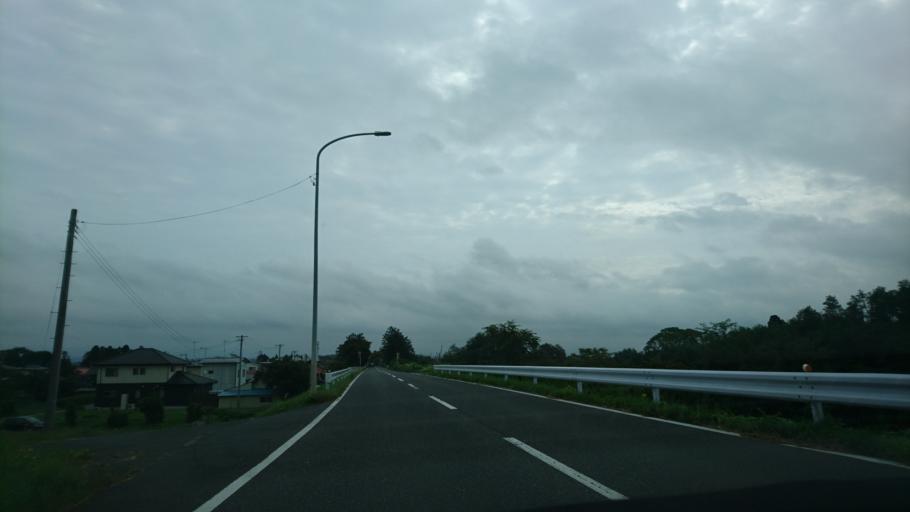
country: JP
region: Iwate
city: Ichinoseki
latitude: 38.7771
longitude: 141.1209
